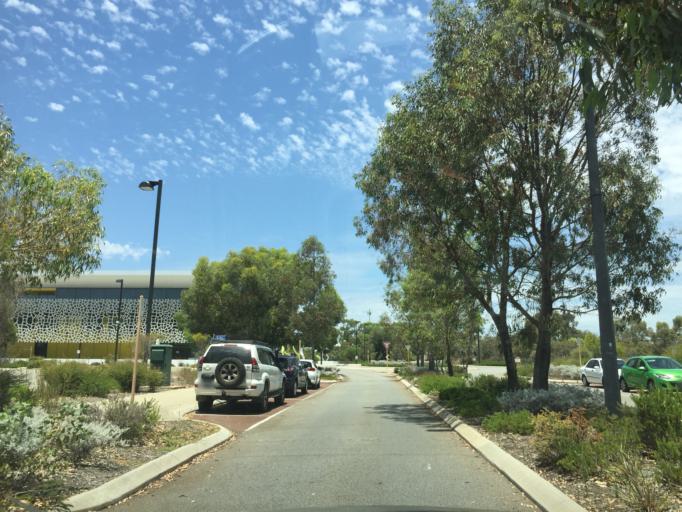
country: AU
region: Western Australia
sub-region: Melville
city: Winthrop
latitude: -32.0726
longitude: 115.8451
